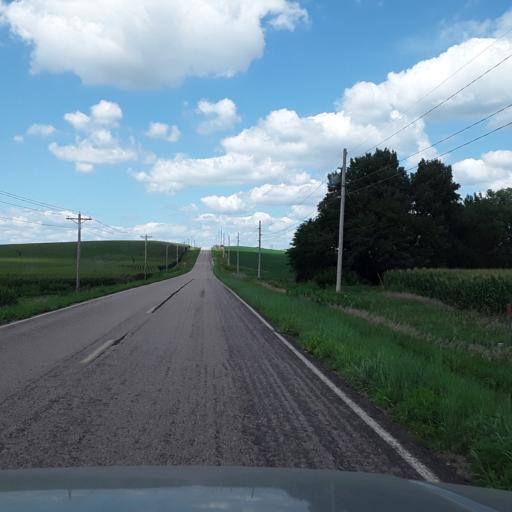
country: US
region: Nebraska
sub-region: Nance County
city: Genoa
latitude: 41.5461
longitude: -97.6960
